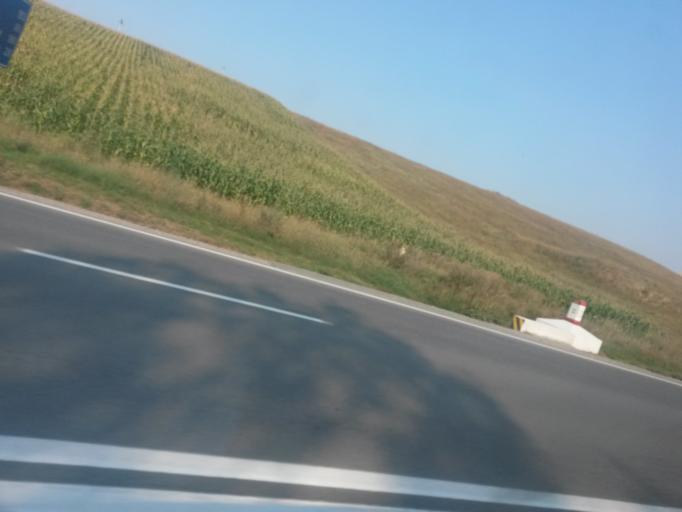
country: RO
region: Cluj
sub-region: Comuna Sandulesti
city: Copaceni
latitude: 46.5905
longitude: 23.7534
